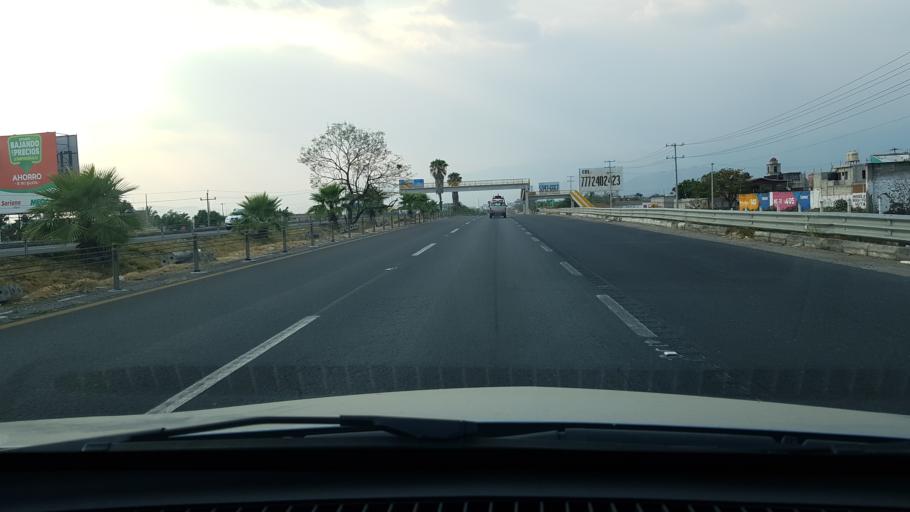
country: MX
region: Morelos
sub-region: Cuautla
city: Tierra Larga (Campo Nuevo)
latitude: 18.8551
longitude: -98.9405
